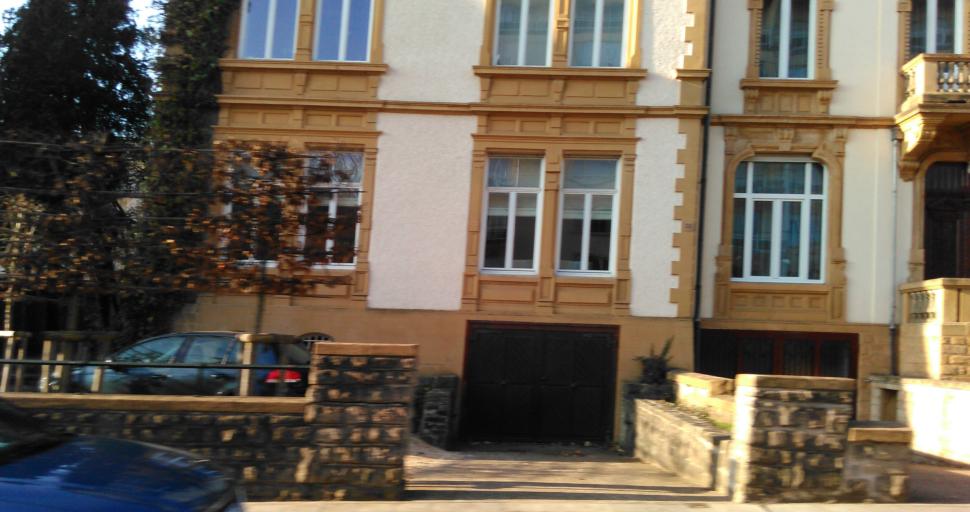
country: LU
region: Luxembourg
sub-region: Canton de Luxembourg
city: Luxembourg
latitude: 49.6109
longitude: 6.1201
